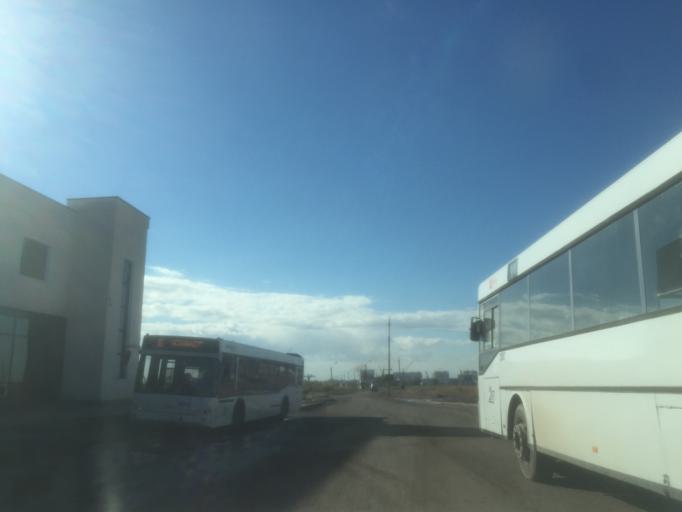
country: KZ
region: Astana Qalasy
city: Astana
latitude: 51.2133
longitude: 71.3549
